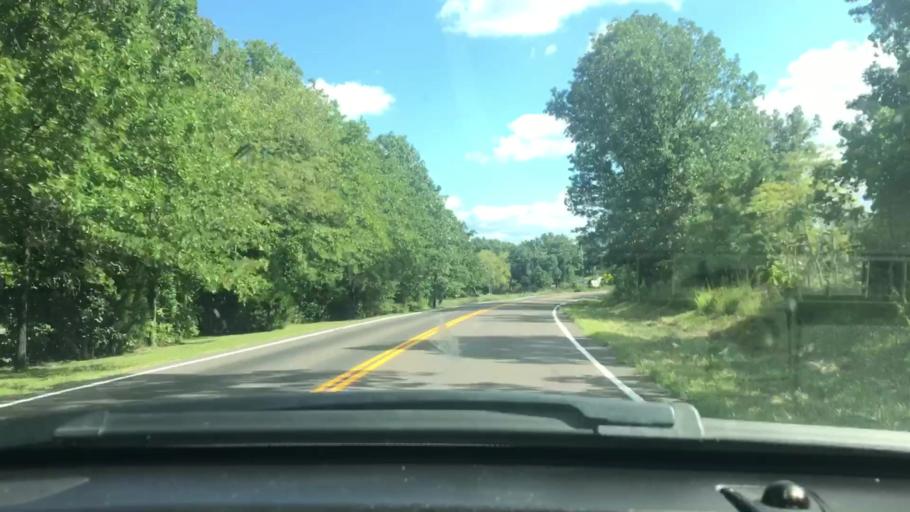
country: US
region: Missouri
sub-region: Wright County
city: Mountain Grove
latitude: 37.2298
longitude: -92.2938
